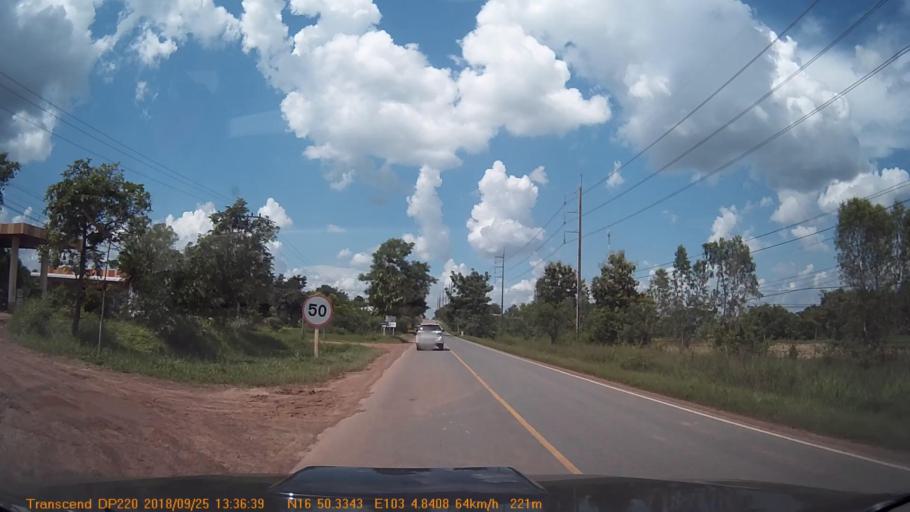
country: TH
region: Khon Kaen
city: Kranuan
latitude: 16.8390
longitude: 103.0807
